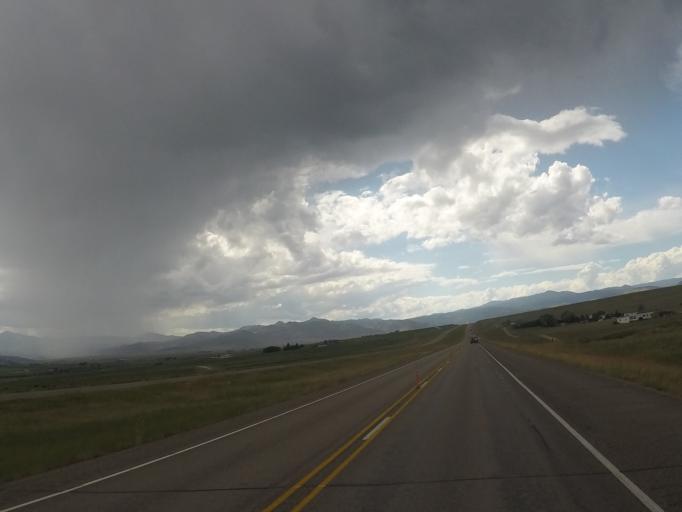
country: US
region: Montana
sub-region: Jefferson County
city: Whitehall
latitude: 45.8858
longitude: -112.1413
